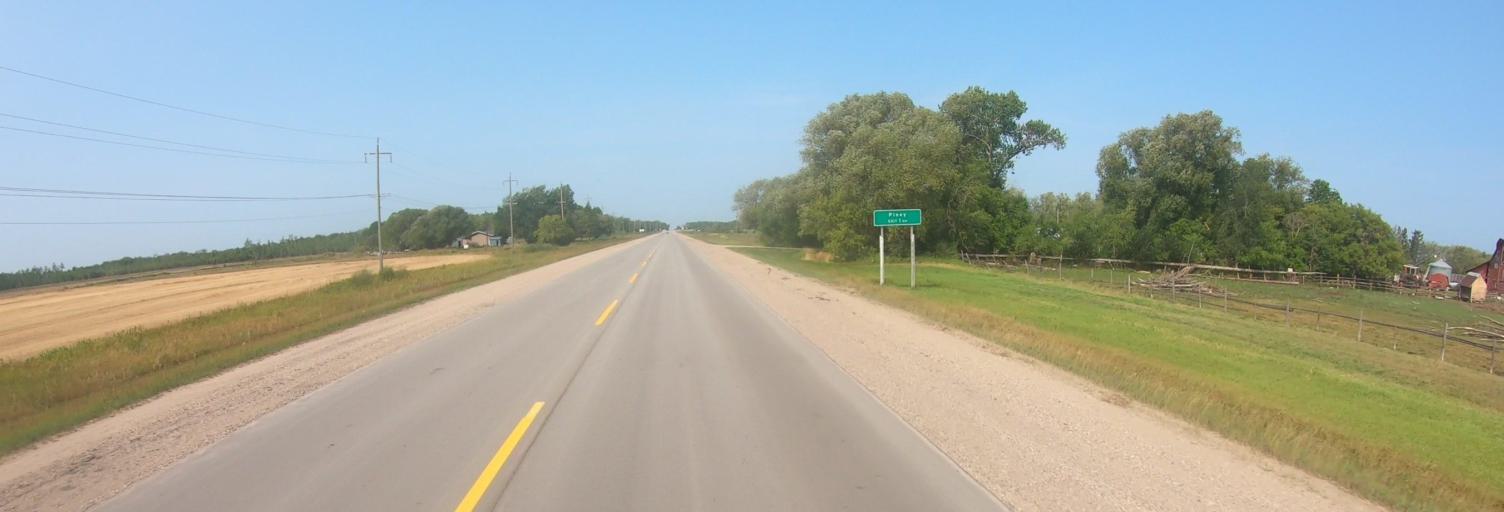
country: US
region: Minnesota
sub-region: Roseau County
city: Roseau
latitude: 49.0896
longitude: -95.9635
